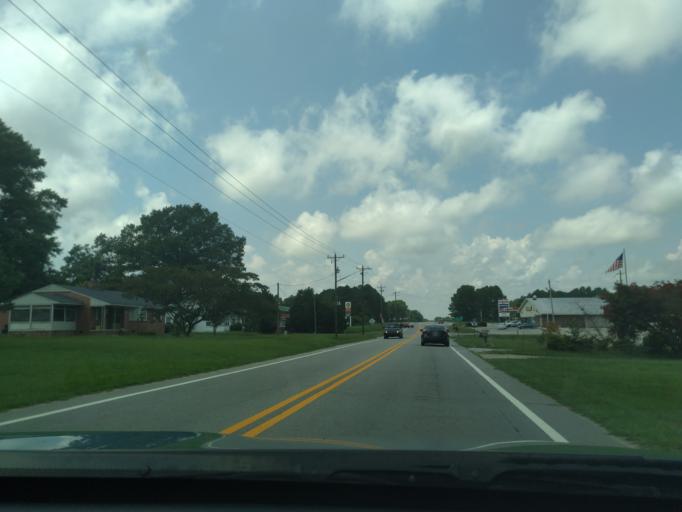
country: US
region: North Carolina
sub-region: Nash County
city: Red Oak
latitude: 36.0121
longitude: -77.8586
